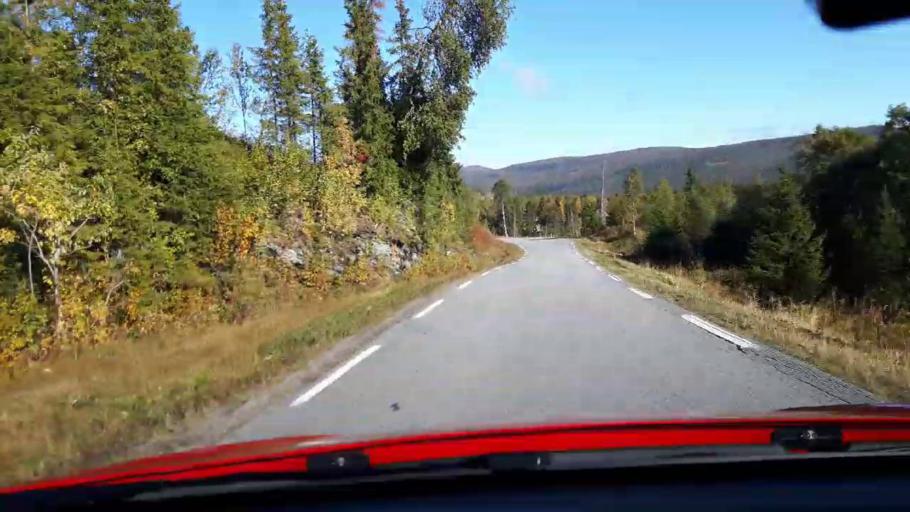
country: NO
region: Nord-Trondelag
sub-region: Lierne
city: Sandvika
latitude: 64.6289
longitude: 13.6904
